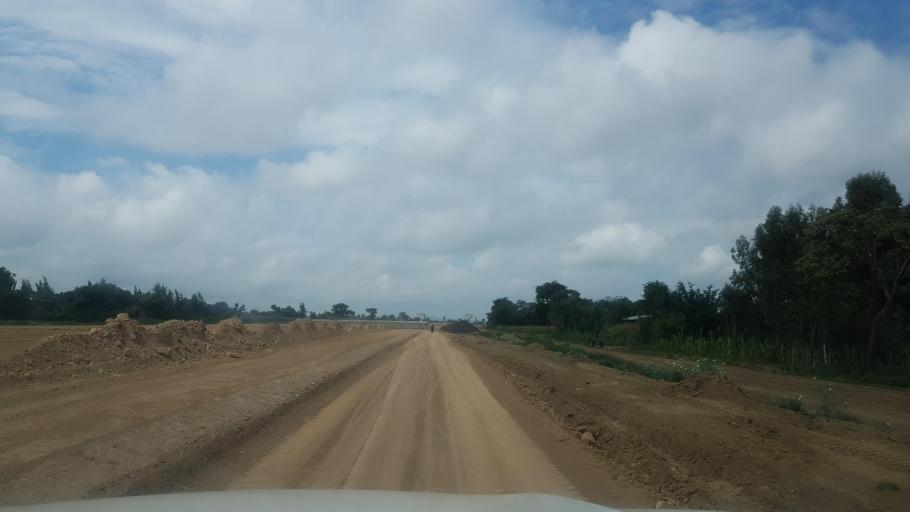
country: ET
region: Oromiya
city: Shashemene
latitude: 7.2621
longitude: 38.5959
